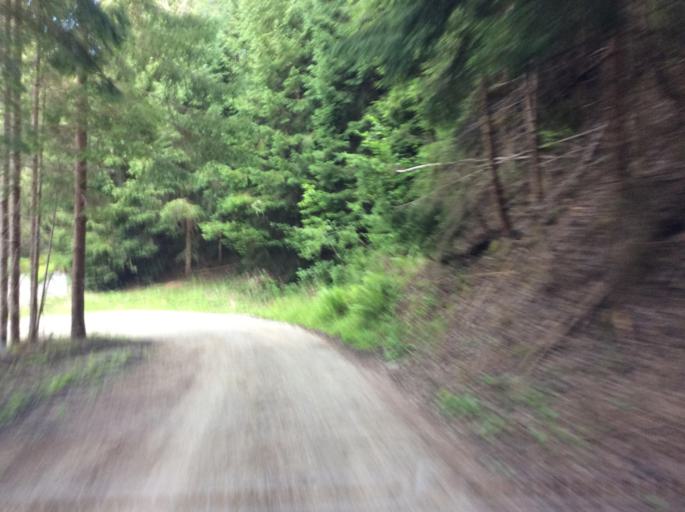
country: AT
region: Salzburg
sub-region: Politischer Bezirk Sankt Johann im Pongau
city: Forstau
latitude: 47.4093
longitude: 13.5730
